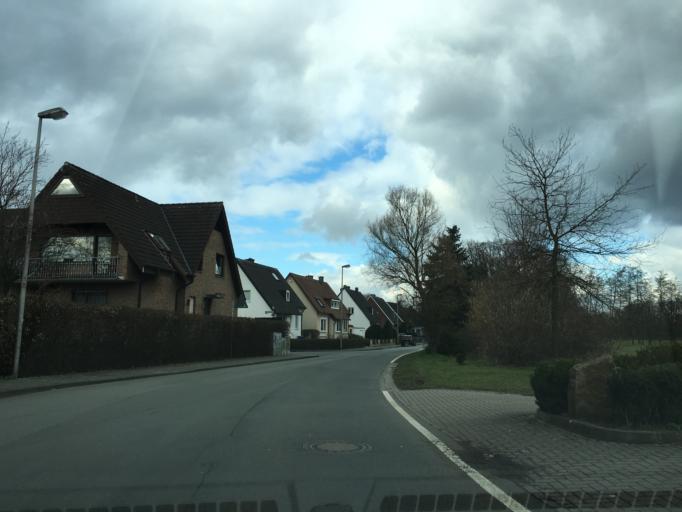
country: DE
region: North Rhine-Westphalia
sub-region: Regierungsbezirk Munster
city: Muenster
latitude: 51.9389
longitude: 7.6579
